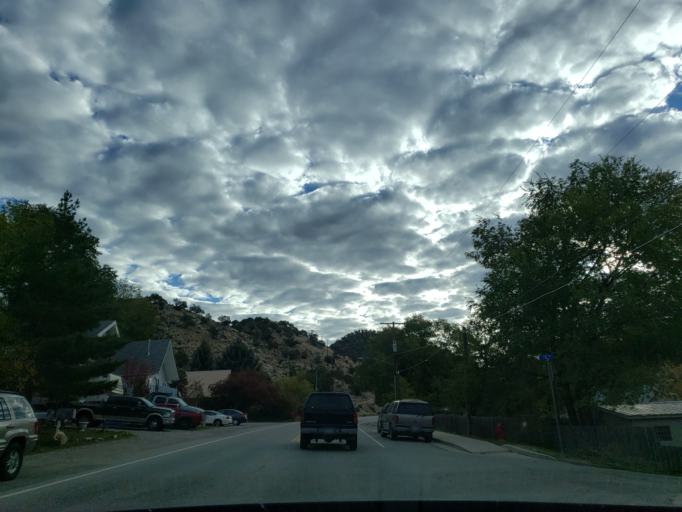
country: US
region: Colorado
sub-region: Garfield County
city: New Castle
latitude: 39.5715
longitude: -107.5268
